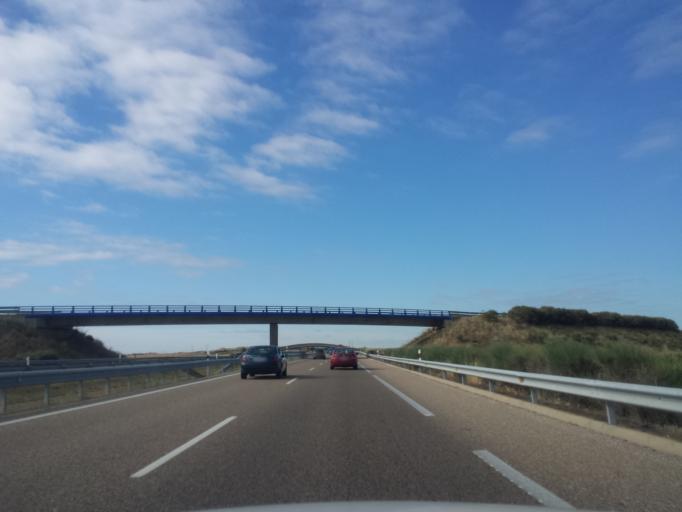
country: ES
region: Castille and Leon
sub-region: Provincia de Leon
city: Villademor de la Vega
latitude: 42.2662
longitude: -5.5916
